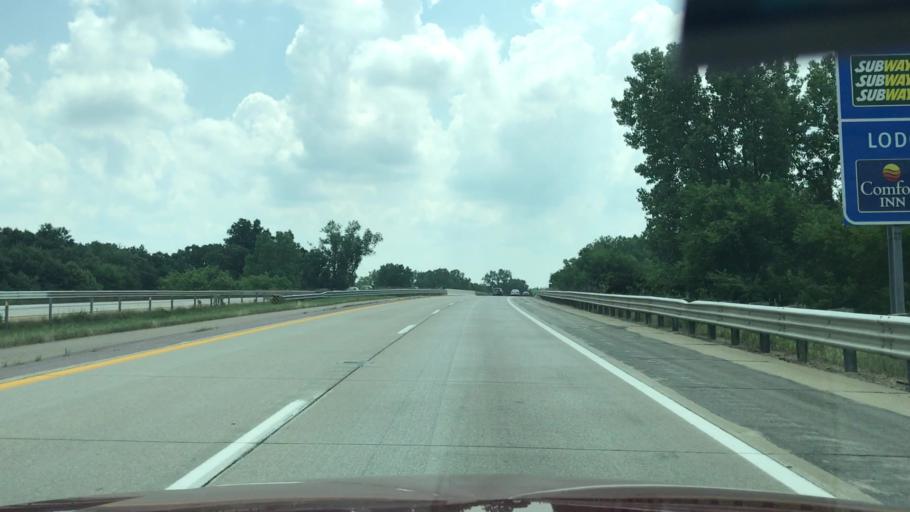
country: US
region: Michigan
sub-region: Allegan County
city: Plainwell
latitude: 42.4603
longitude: -85.6527
